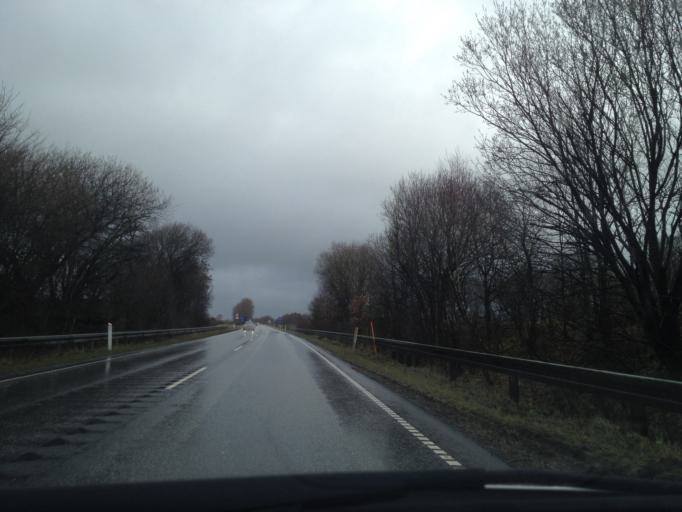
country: DK
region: South Denmark
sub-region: Kolding Kommune
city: Vamdrup
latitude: 55.4120
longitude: 9.2946
